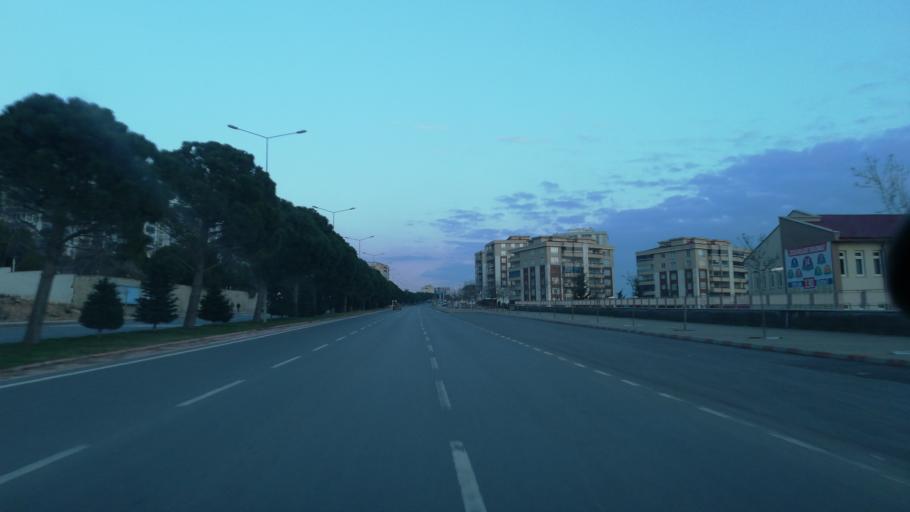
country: TR
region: Kahramanmaras
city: Kahramanmaras
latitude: 37.5985
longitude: 36.8416
